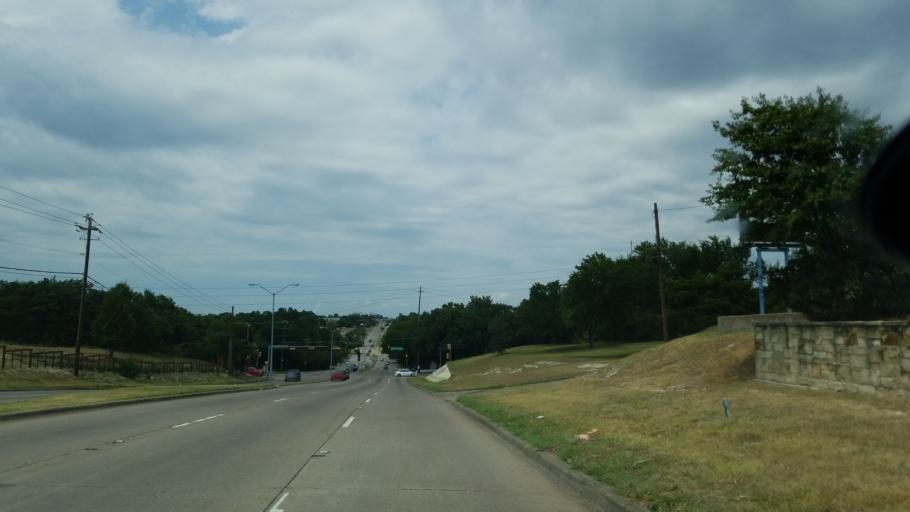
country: US
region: Texas
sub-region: Dallas County
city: Duncanville
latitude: 32.6607
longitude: -96.8570
